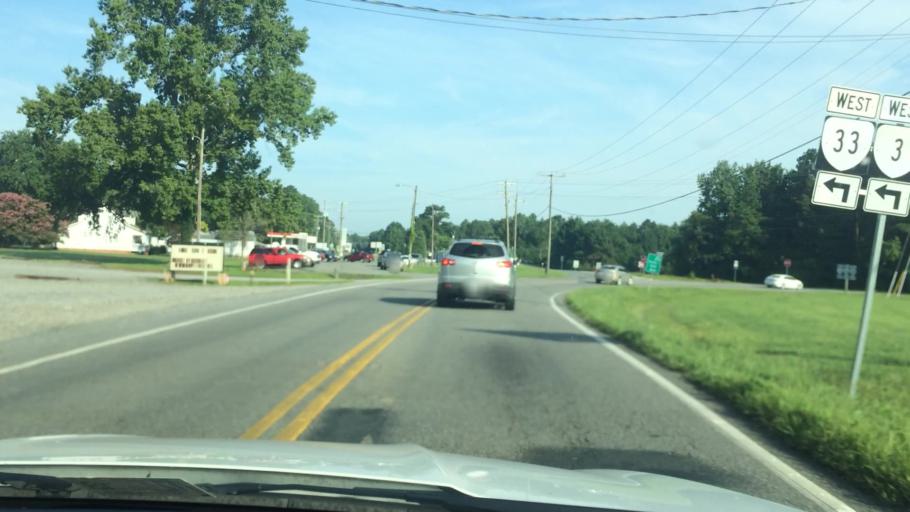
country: US
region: Virginia
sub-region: Middlesex County
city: Deltaville
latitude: 37.5498
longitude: -76.4432
